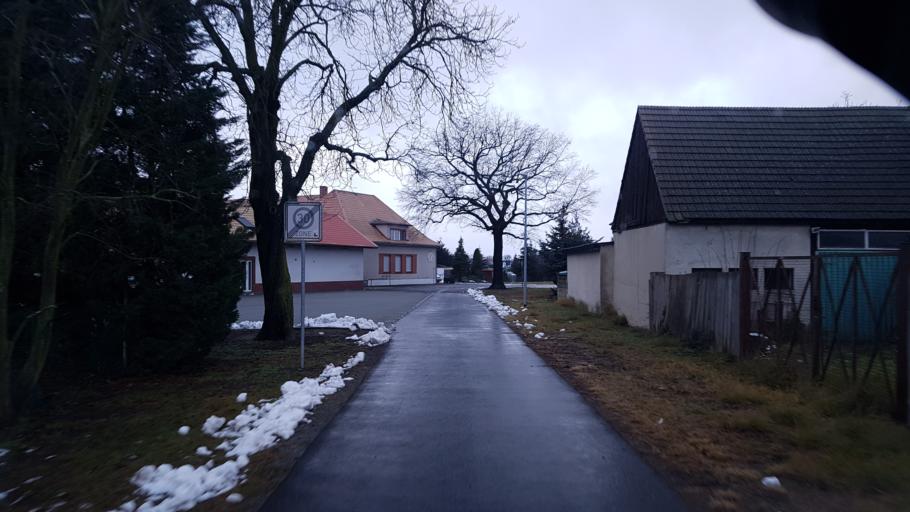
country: DE
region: Brandenburg
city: Janschwalde
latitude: 51.8633
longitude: 14.5103
